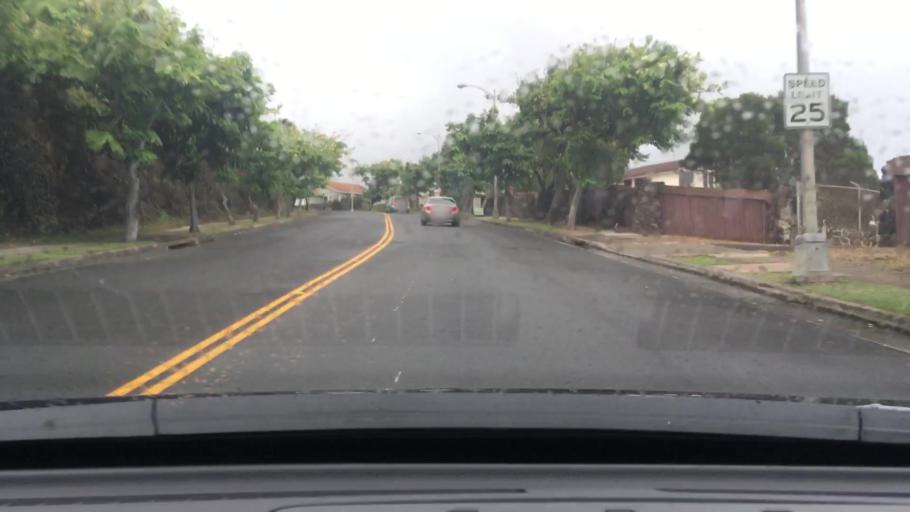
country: US
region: Hawaii
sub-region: Honolulu County
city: Waimanalo Beach
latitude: 21.2907
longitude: -157.7037
